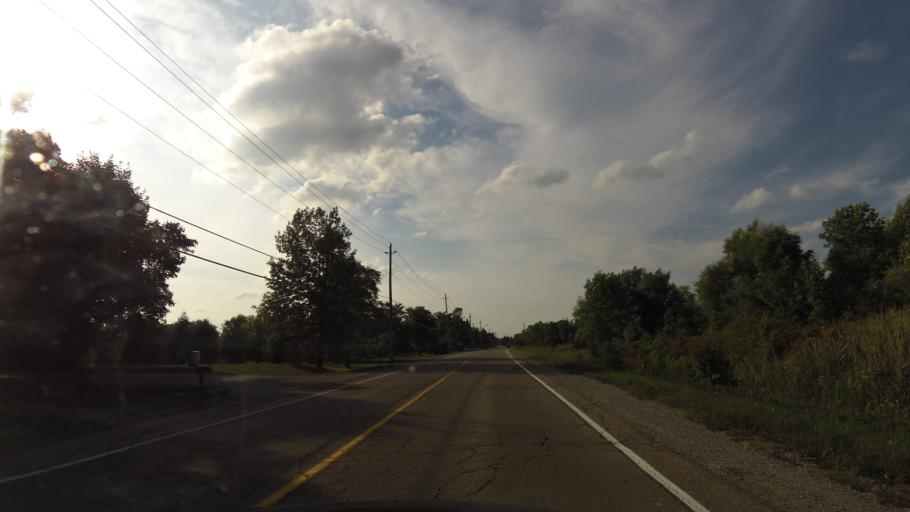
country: CA
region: Ontario
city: Burlington
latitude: 43.3757
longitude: -79.8721
